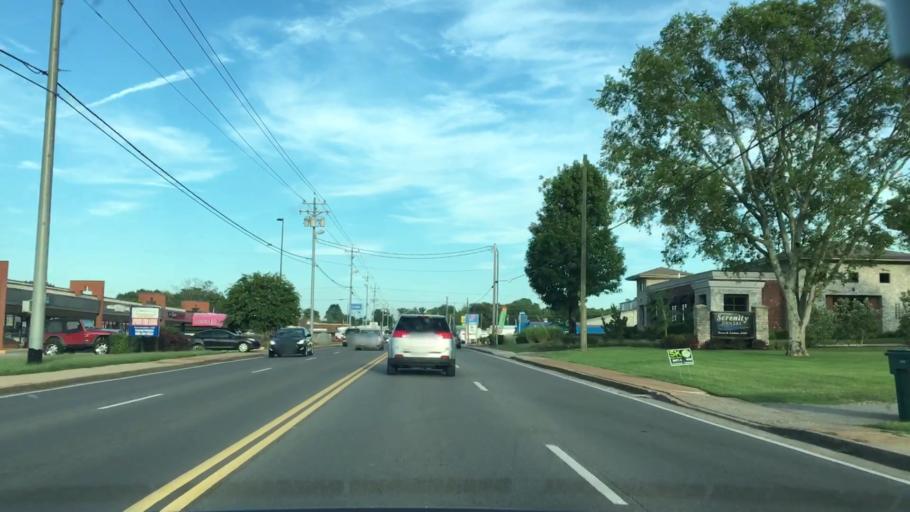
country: US
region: Tennessee
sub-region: Wilson County
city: Lebanon
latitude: 36.2119
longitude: -86.3170
